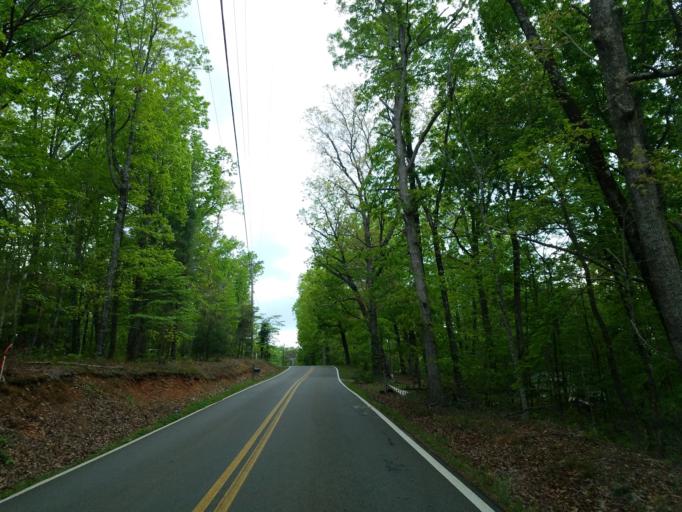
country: US
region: Georgia
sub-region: Pickens County
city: Jasper
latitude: 34.4409
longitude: -84.4729
